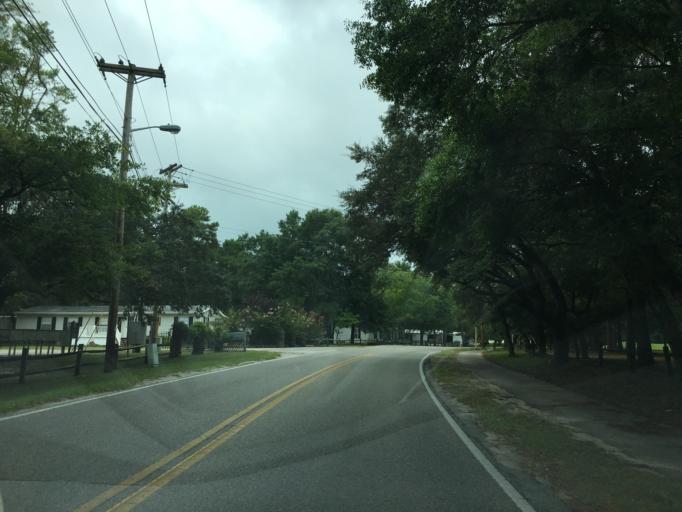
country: US
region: South Carolina
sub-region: Horry County
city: North Myrtle Beach
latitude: 33.7790
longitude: -78.7718
